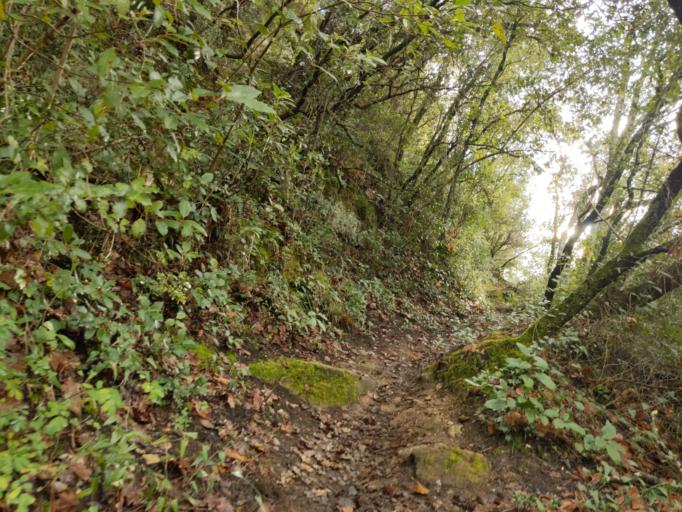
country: FR
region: Provence-Alpes-Cote d'Azur
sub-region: Departement du Var
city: Bagnols-en-Foret
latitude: 43.5400
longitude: 6.7057
